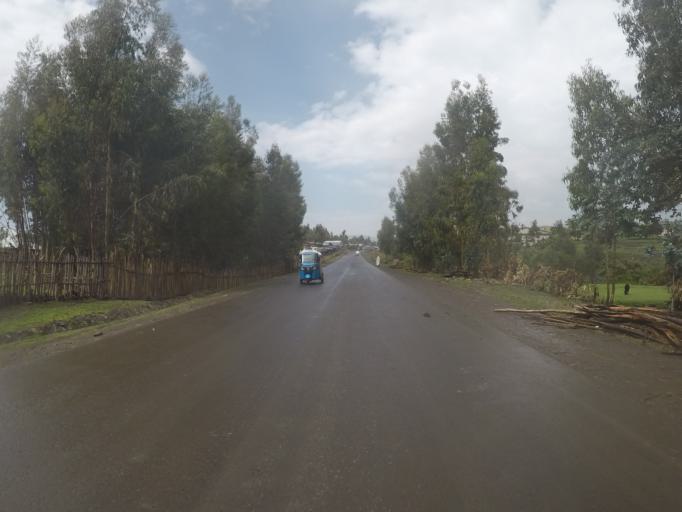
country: ET
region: Amhara
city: Debark'
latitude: 13.1226
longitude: 37.8835
